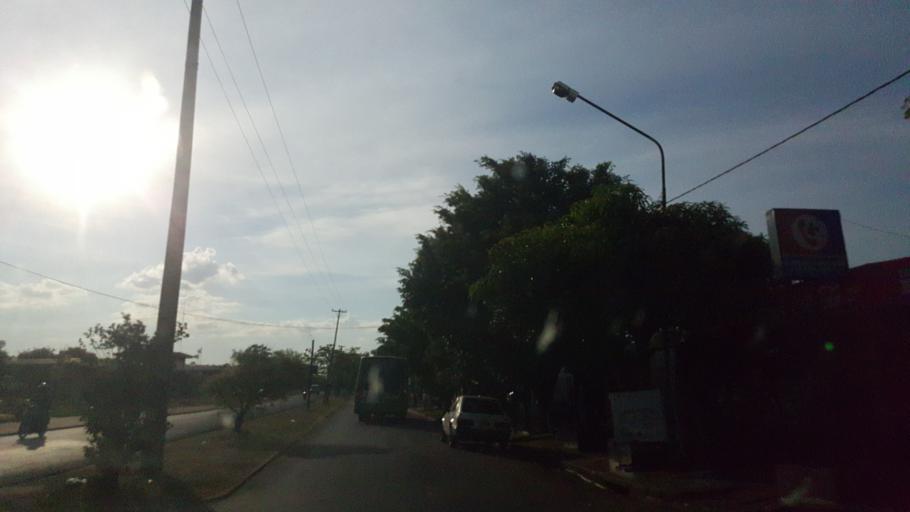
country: AR
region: Misiones
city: Garupa
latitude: -27.4343
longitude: -55.8716
